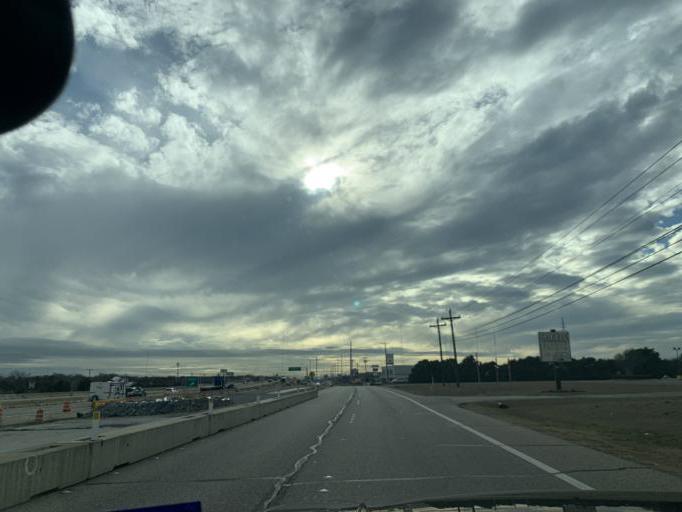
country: US
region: Texas
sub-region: Dallas County
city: Shamrock
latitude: 32.6132
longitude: -96.9226
